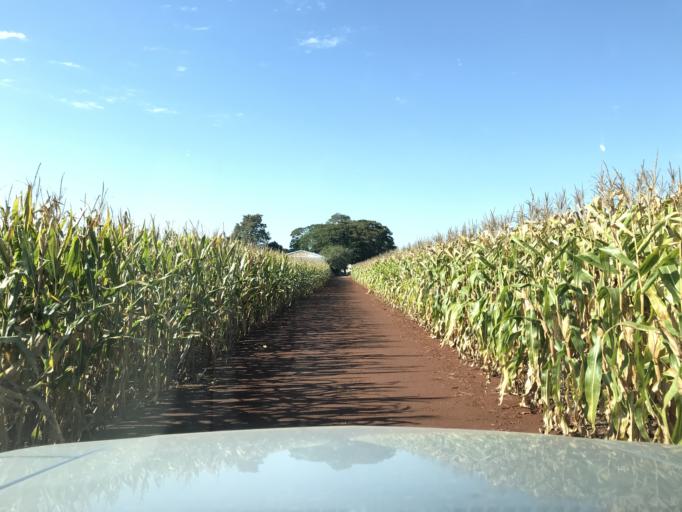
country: BR
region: Parana
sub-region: Palotina
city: Palotina
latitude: -24.2640
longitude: -53.8059
